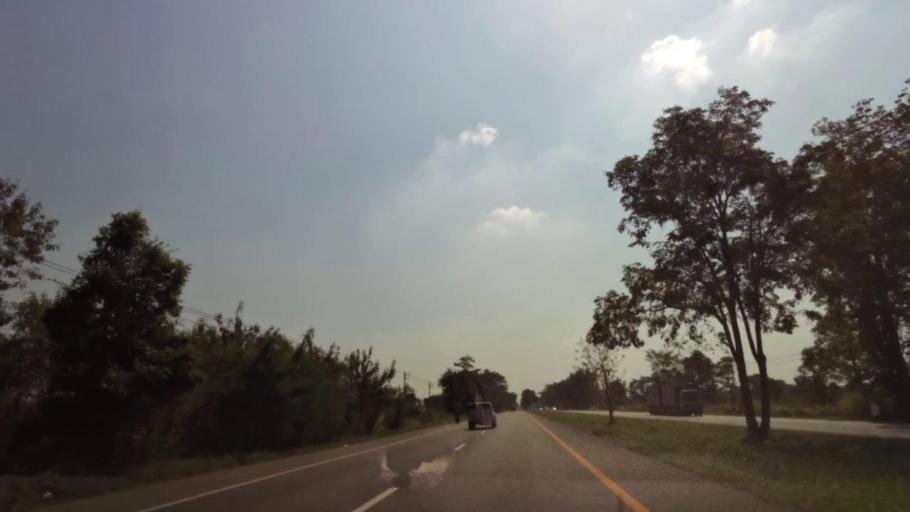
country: TH
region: Phichit
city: Bueng Na Rang
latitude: 16.2269
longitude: 100.1261
